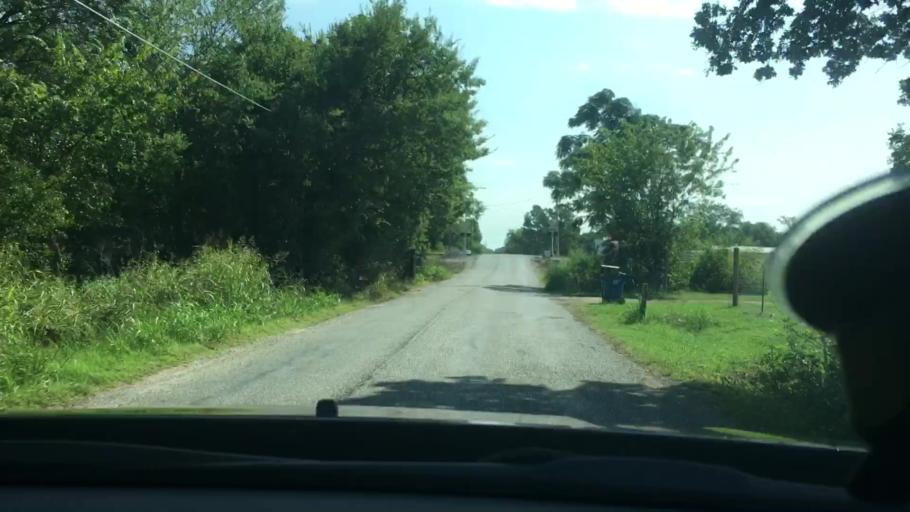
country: US
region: Oklahoma
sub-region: Bryan County
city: Colbert
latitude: 33.9110
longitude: -96.5334
